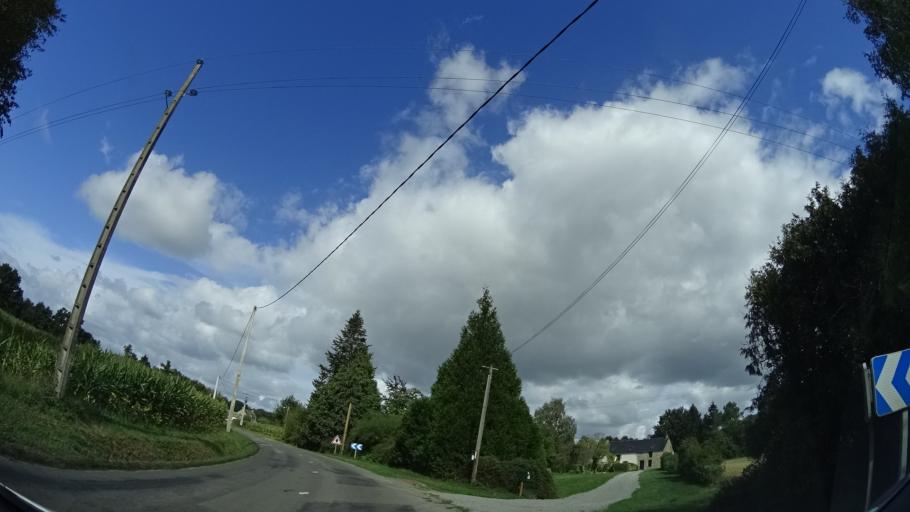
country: FR
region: Brittany
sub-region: Departement d'Ille-et-Vilaine
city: Montreuil-sur-Ille
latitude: 48.3325
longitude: -1.6867
